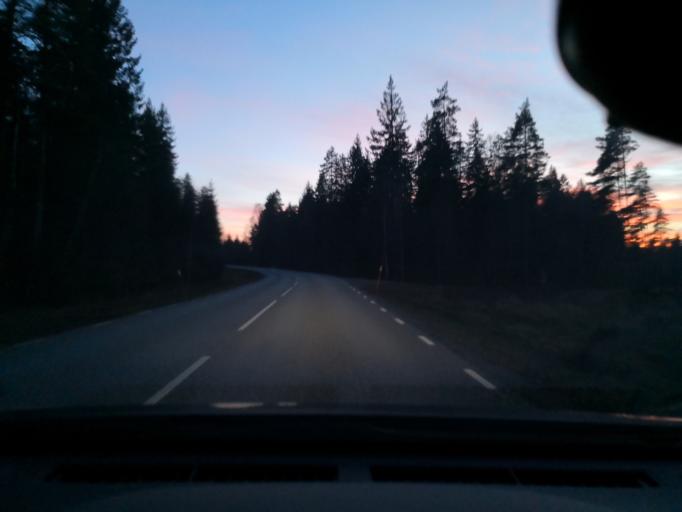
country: SE
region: OErebro
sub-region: Lindesbergs Kommun
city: Frovi
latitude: 59.3888
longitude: 15.4412
